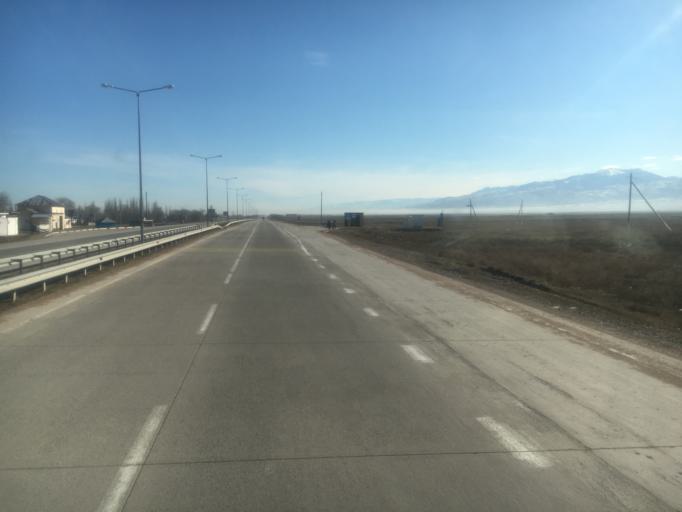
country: KZ
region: Zhambyl
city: Merke
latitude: 42.8893
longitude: 72.9836
